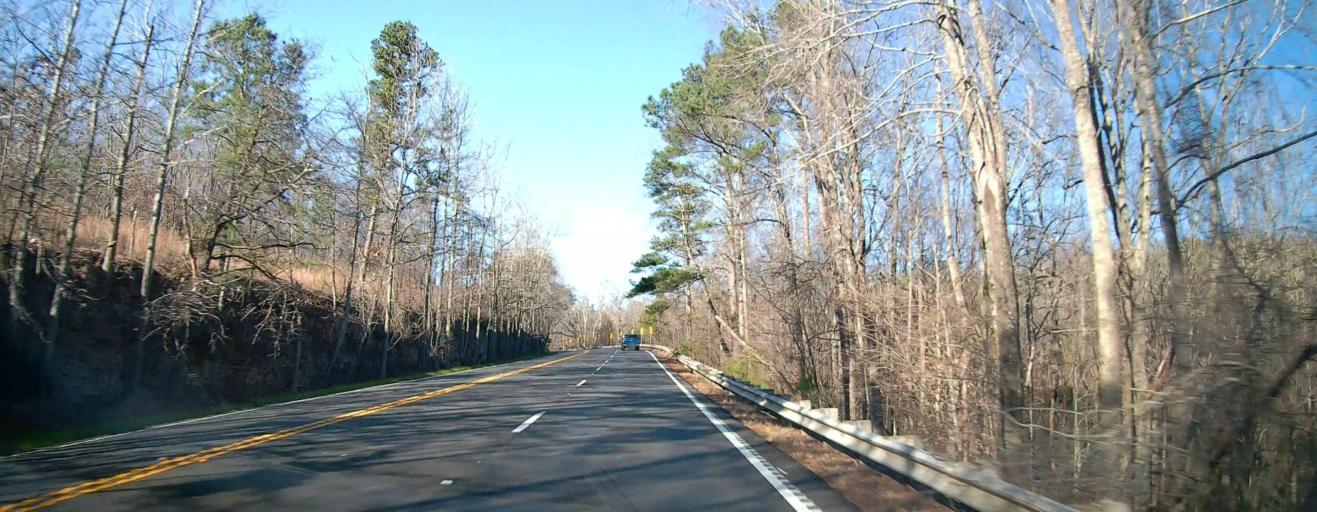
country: US
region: Georgia
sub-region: Talbot County
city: Sardis
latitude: 32.8424
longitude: -84.6948
